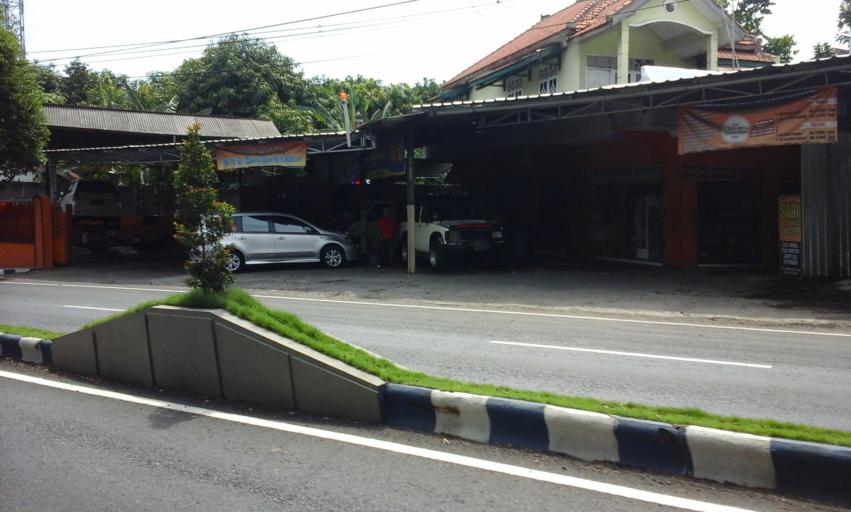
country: ID
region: East Java
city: Cungking
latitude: -8.2204
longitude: 114.3527
